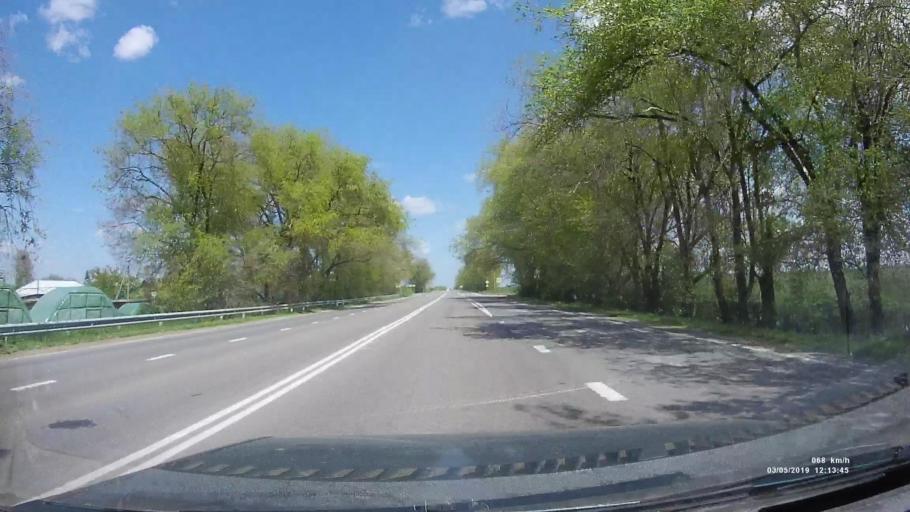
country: RU
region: Rostov
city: Melikhovskaya
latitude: 47.3358
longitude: 40.5572
